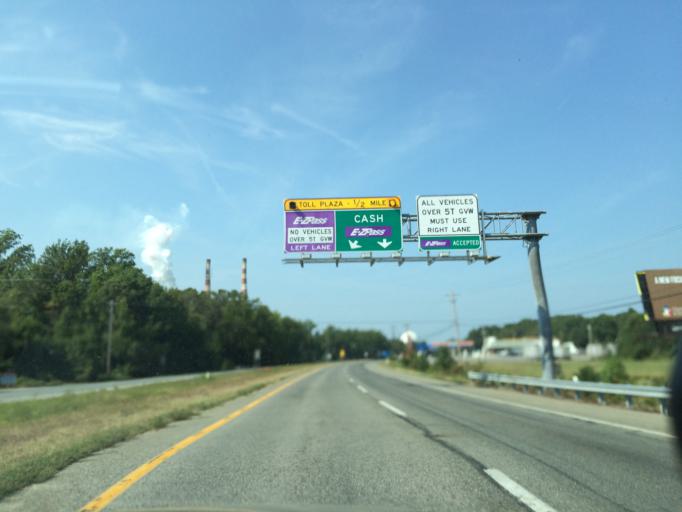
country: US
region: Virginia
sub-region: King George County
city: Dahlgren
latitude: 38.3672
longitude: -76.9651
